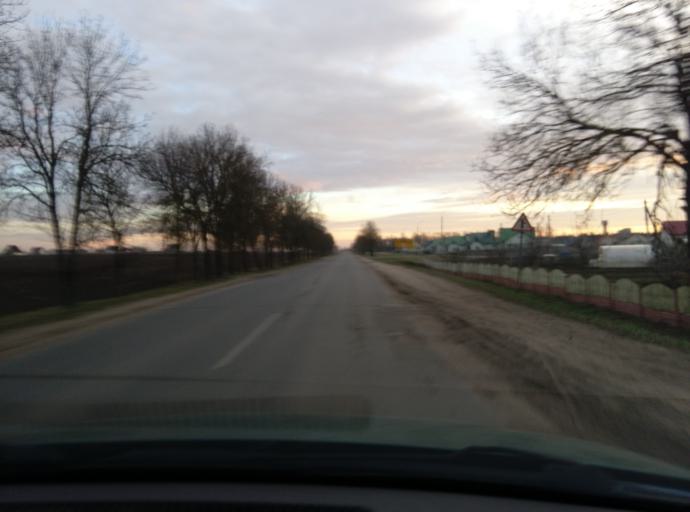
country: BY
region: Minsk
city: Horad Barysaw
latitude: 54.2791
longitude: 28.4948
